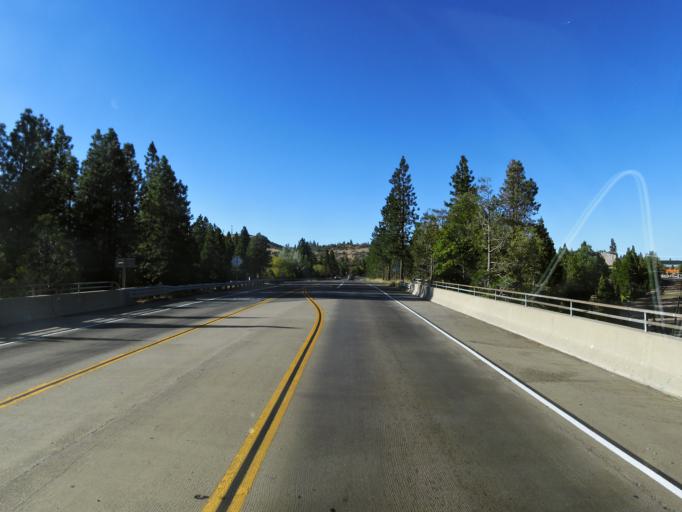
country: US
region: California
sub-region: Siskiyou County
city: Weed
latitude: 41.4244
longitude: -122.3880
